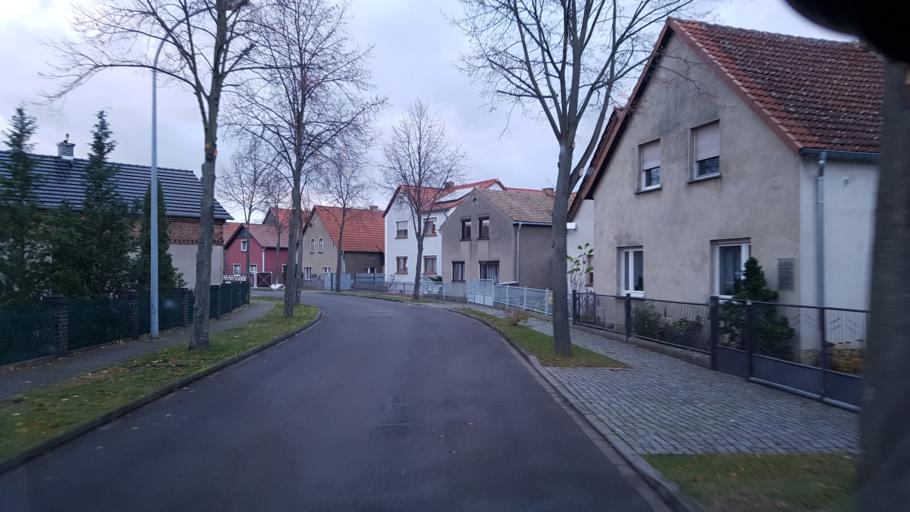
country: DE
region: Brandenburg
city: Tettau
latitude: 51.4332
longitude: 13.7259
